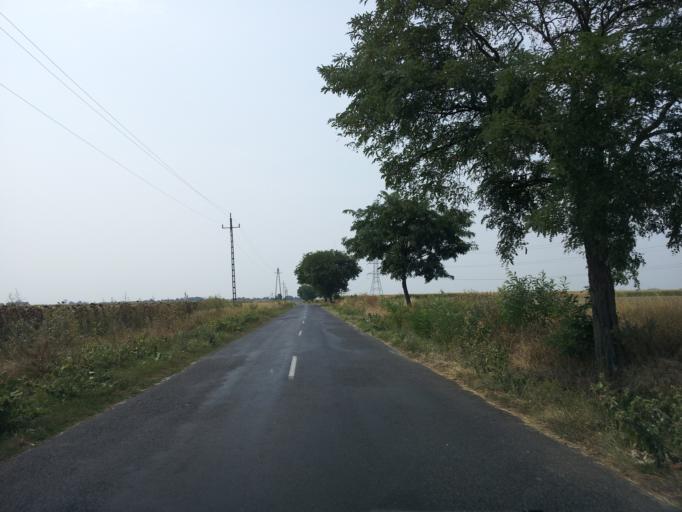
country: HU
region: Gyor-Moson-Sopron
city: Mihalyi
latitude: 47.5094
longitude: 17.1478
